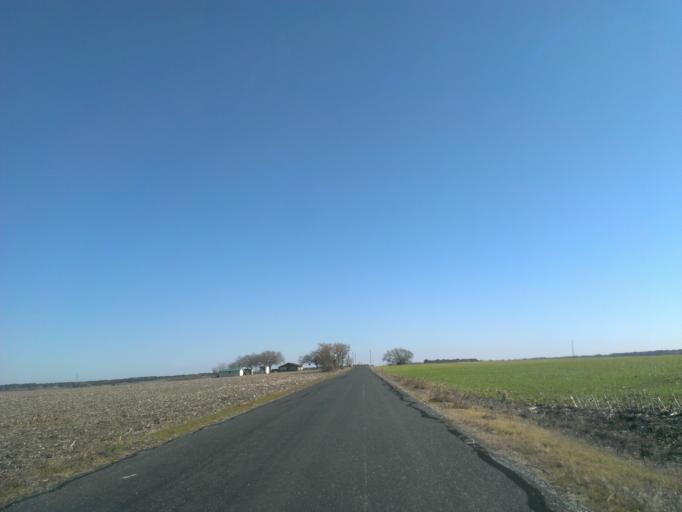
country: US
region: Texas
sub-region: Williamson County
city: Georgetown
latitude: 30.6555
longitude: -97.5717
